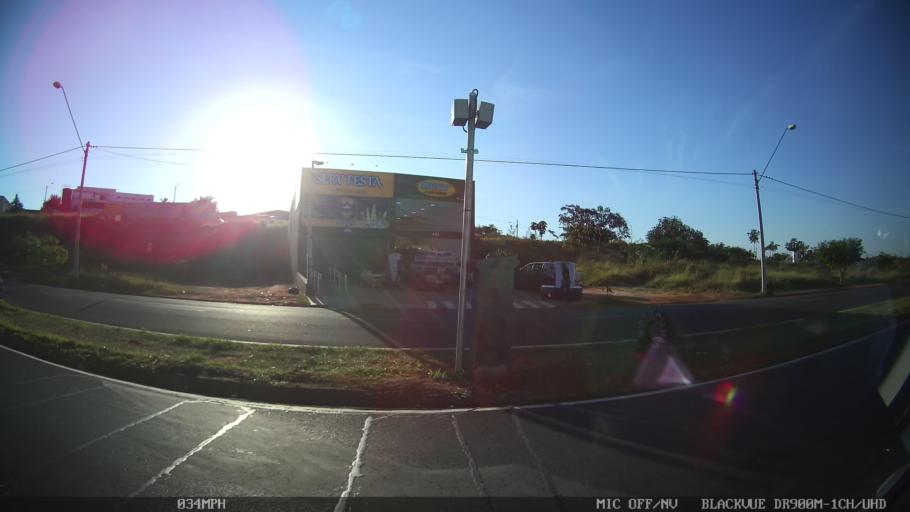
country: BR
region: Sao Paulo
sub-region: Sao Jose Do Rio Preto
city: Sao Jose do Rio Preto
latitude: -20.7918
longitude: -49.3508
